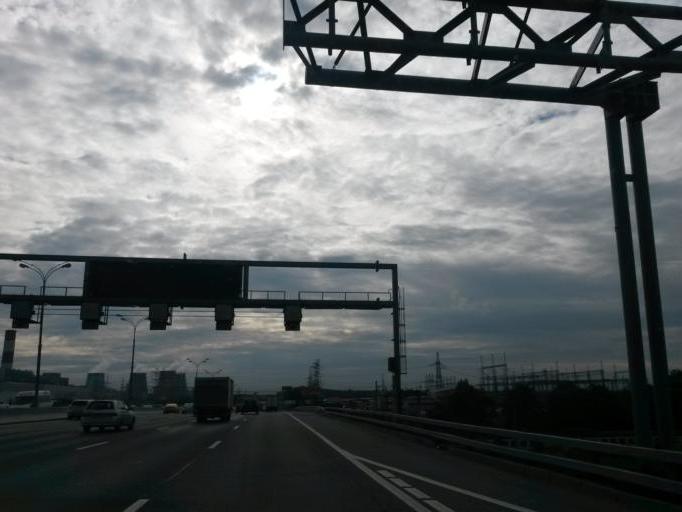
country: RU
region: Moscow
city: Annino
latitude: 55.5750
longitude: 37.6117
